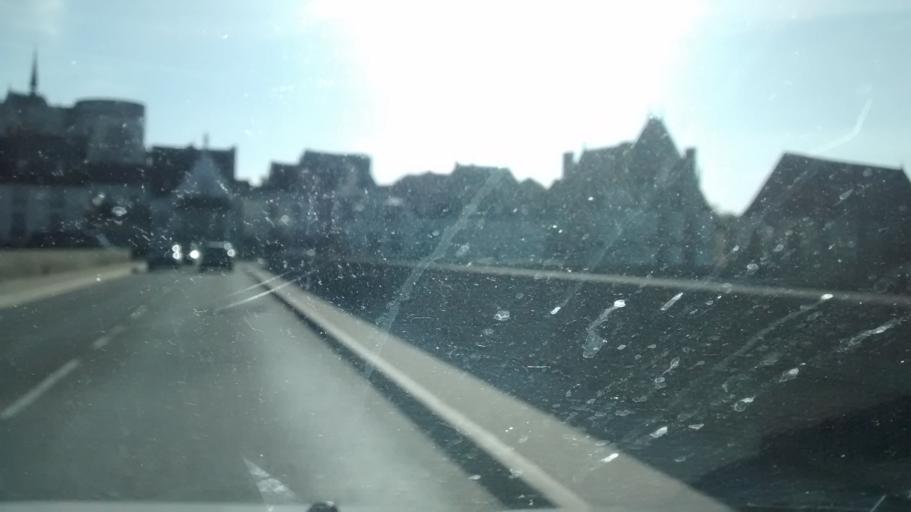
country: FR
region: Centre
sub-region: Departement d'Indre-et-Loire
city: Amboise
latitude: 47.4144
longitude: 0.9839
